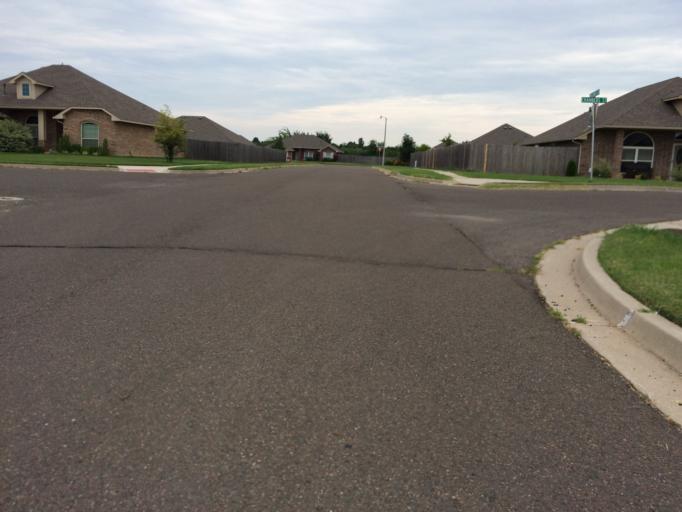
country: US
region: Oklahoma
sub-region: Cleveland County
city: Hall Park
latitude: 35.2446
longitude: -97.4184
